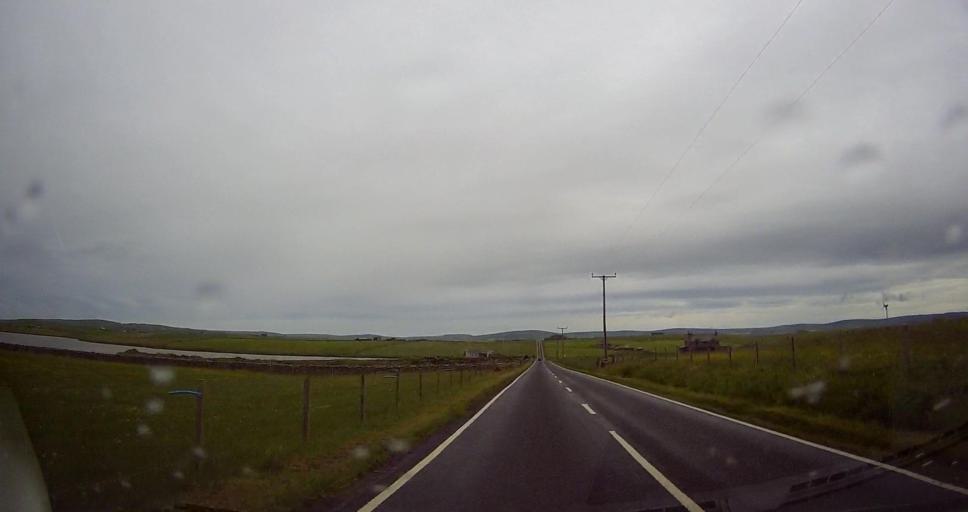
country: GB
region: Scotland
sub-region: Orkney Islands
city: Stromness
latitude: 59.0230
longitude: -3.2967
